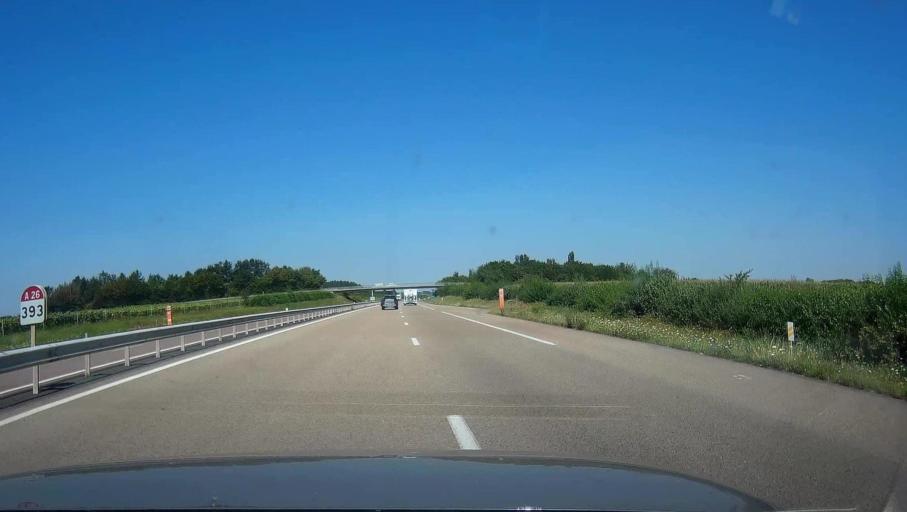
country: FR
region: Champagne-Ardenne
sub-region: Departement de l'Aube
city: Verrieres
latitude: 48.2395
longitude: 4.1722
